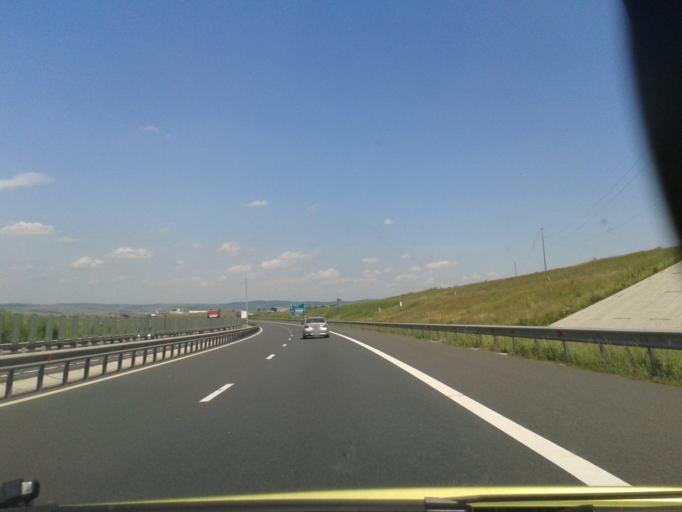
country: RO
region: Sibiu
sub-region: Comuna Cristian
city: Cristian
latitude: 45.8025
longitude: 24.0516
